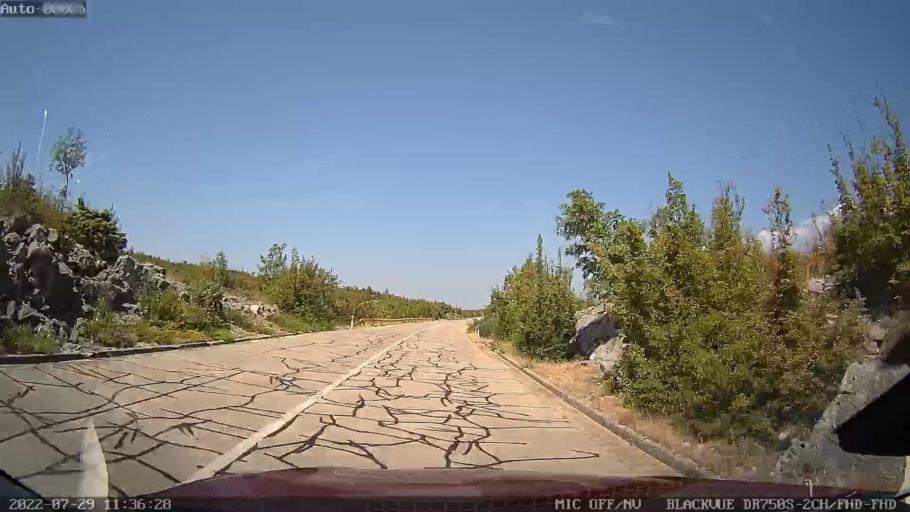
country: HR
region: Zadarska
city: Obrovac
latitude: 44.1897
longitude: 15.6977
